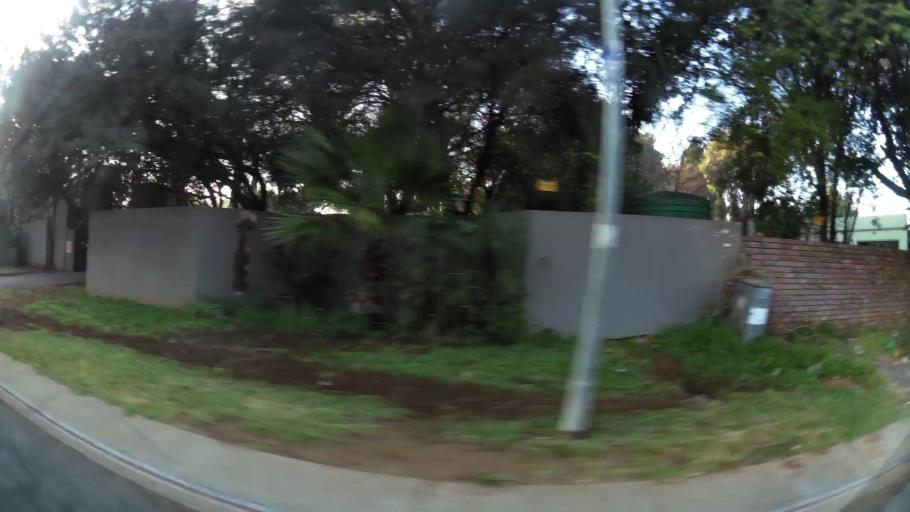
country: ZA
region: Orange Free State
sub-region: Mangaung Metropolitan Municipality
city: Bloemfontein
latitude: -29.0840
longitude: 26.1571
